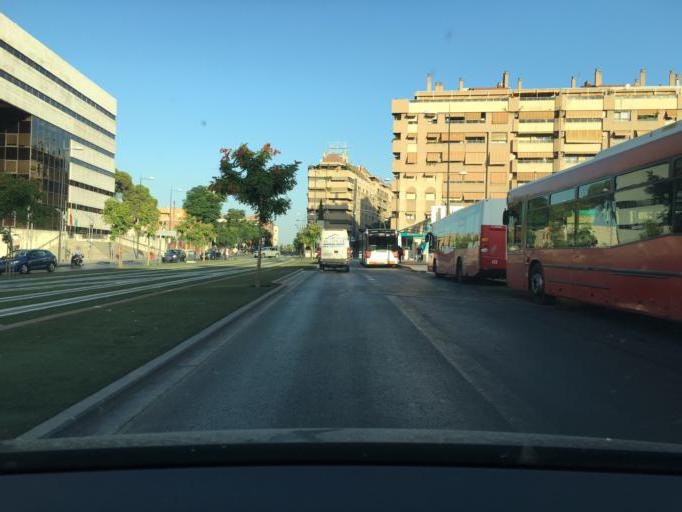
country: ES
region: Andalusia
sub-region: Provincia de Granada
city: Granada
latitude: 37.1870
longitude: -3.6101
